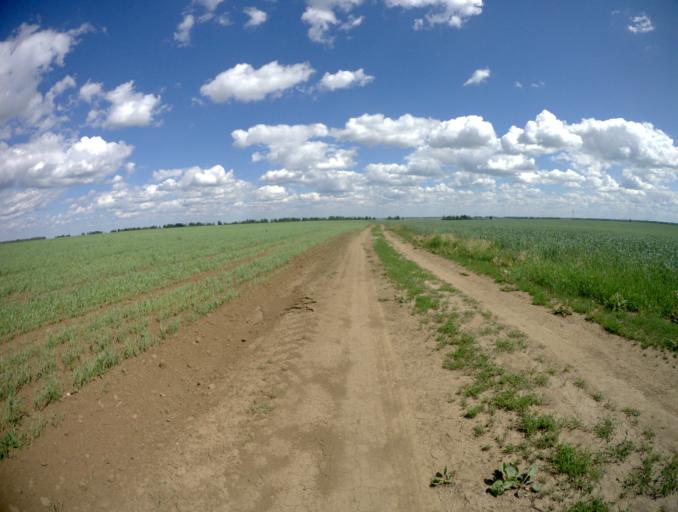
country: RU
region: Vladimir
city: Suzdal'
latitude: 56.4347
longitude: 40.3326
